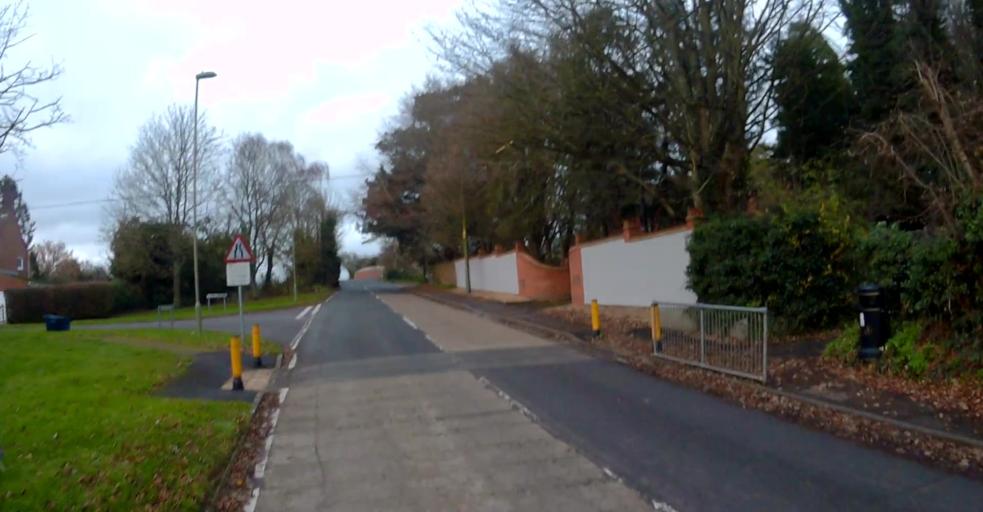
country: GB
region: England
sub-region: Hampshire
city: Overton
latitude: 51.2522
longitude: -1.2641
